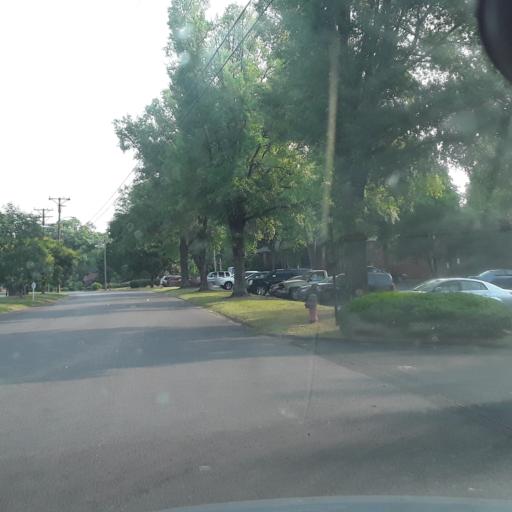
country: US
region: Tennessee
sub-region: Williamson County
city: Brentwood
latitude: 36.0568
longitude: -86.7193
